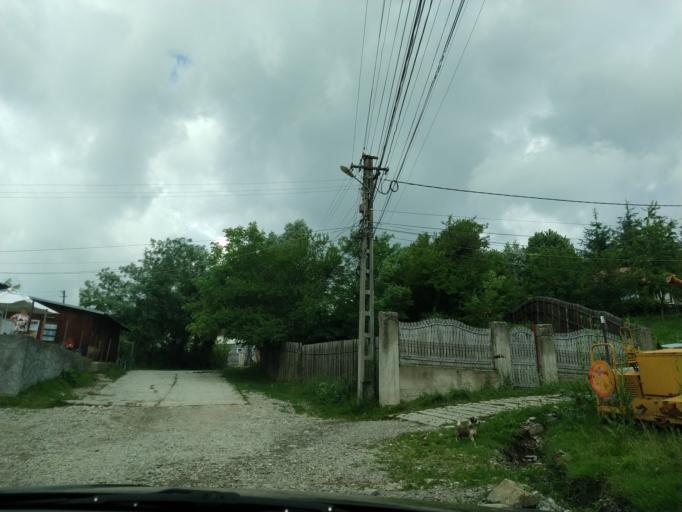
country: RO
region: Prahova
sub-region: Oras Breaza
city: Valea Tarsei
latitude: 45.1850
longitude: 25.6301
